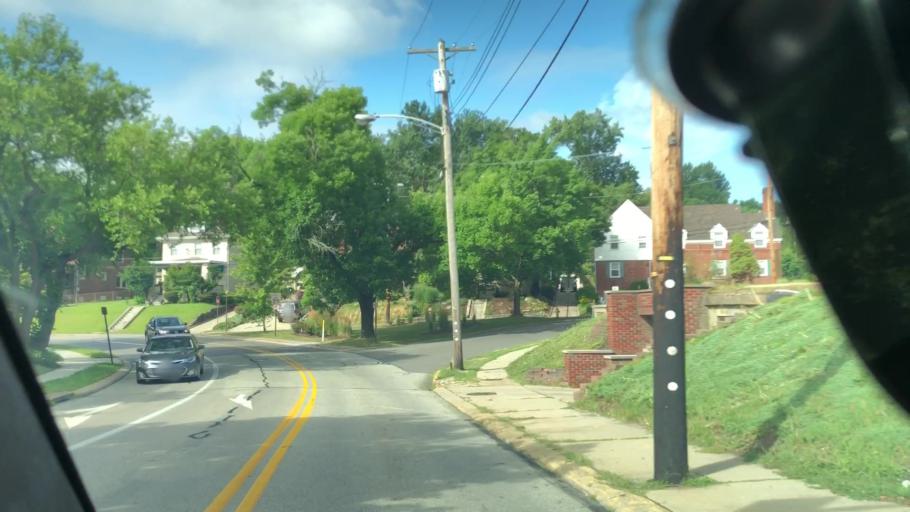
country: US
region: Pennsylvania
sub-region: Allegheny County
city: Dormont
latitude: 40.3934
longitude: -80.0467
